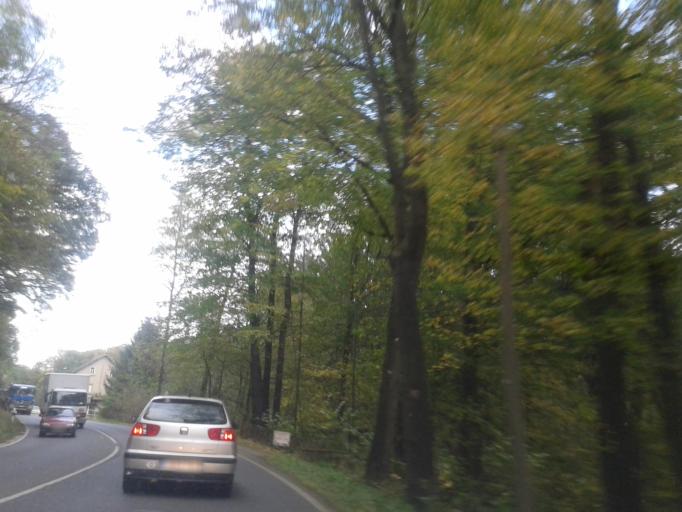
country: DE
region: Saxony
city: Niederschona
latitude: 51.0117
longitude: 13.4728
